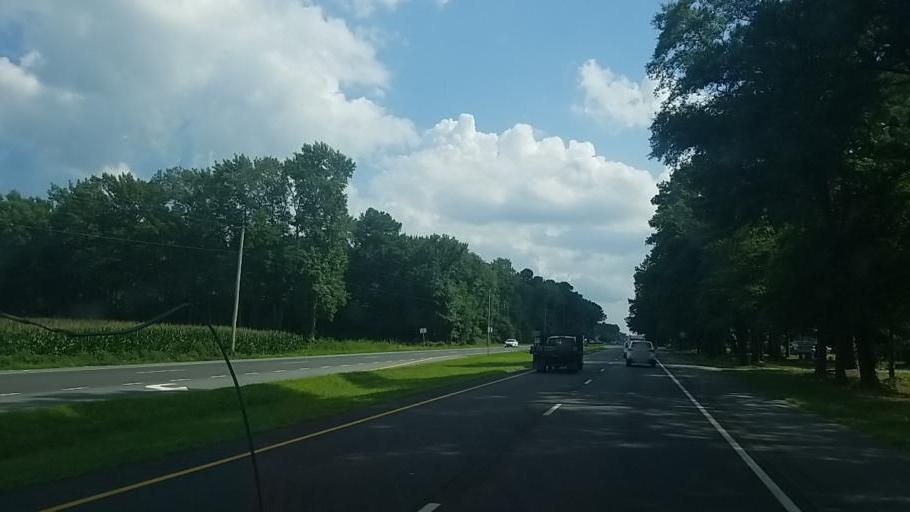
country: US
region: Delaware
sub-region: Sussex County
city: Selbyville
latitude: 38.4742
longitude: -75.2350
